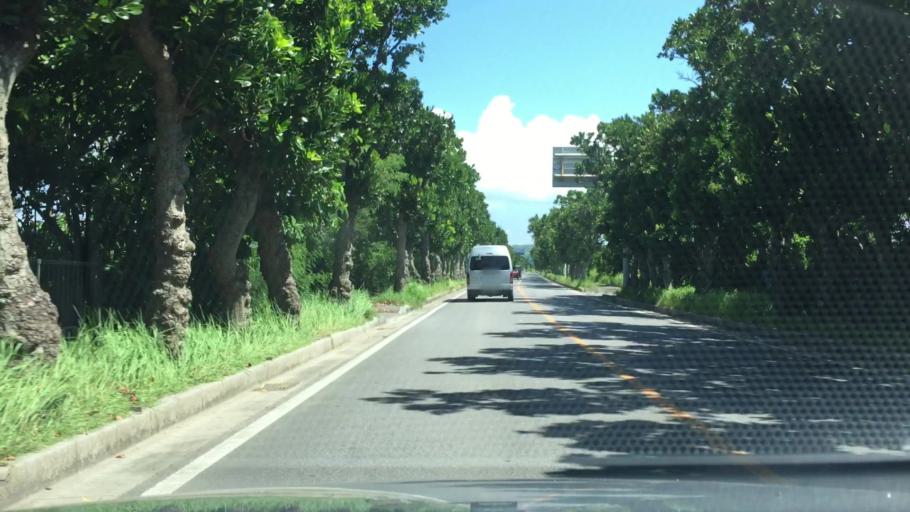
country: JP
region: Okinawa
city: Ishigaki
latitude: 24.3714
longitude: 124.2462
